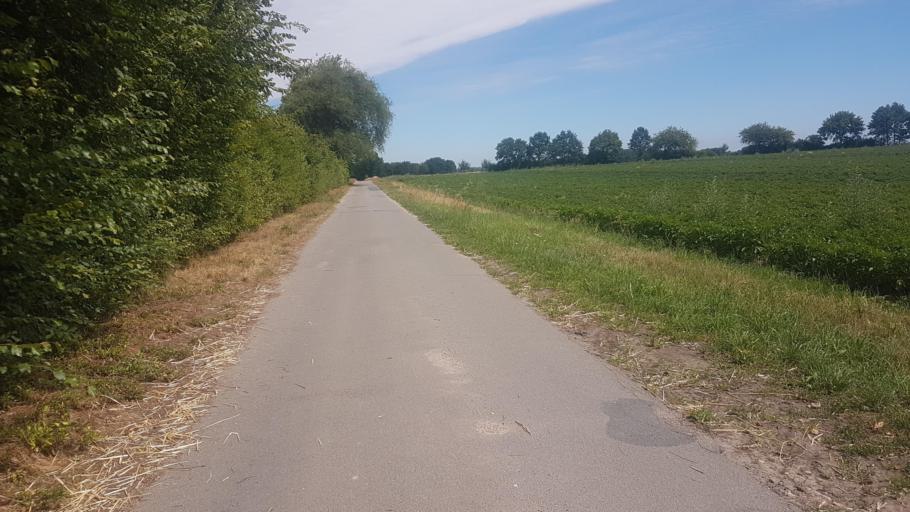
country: DE
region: Lower Saxony
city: Bleckede
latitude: 53.2621
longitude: 10.7633
